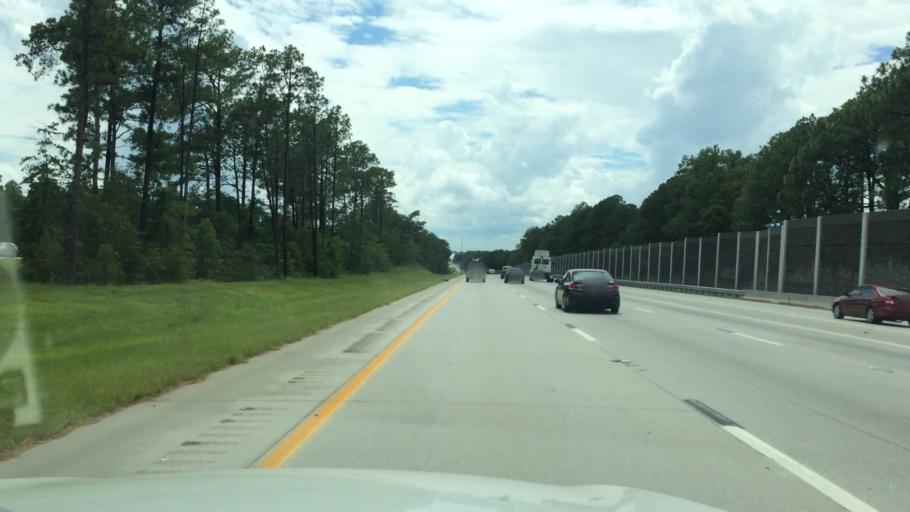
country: US
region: South Carolina
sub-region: Richland County
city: Woodfield
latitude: 34.0939
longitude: -80.8589
